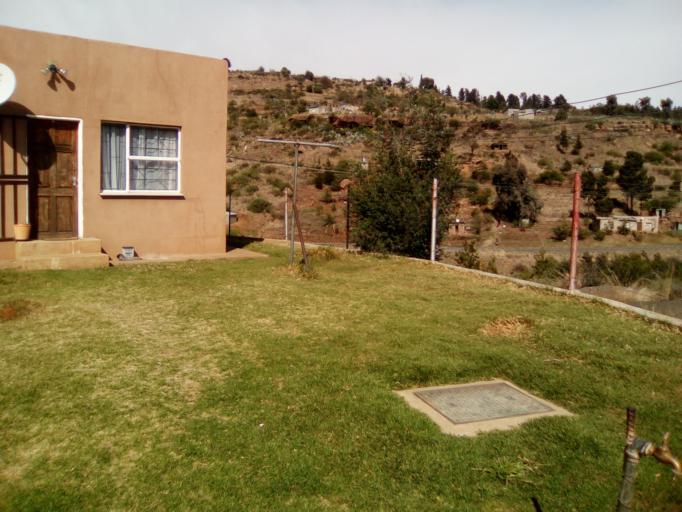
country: LS
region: Qacha's Nek
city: Qacha's Nek
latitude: -30.0968
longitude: 28.6503
